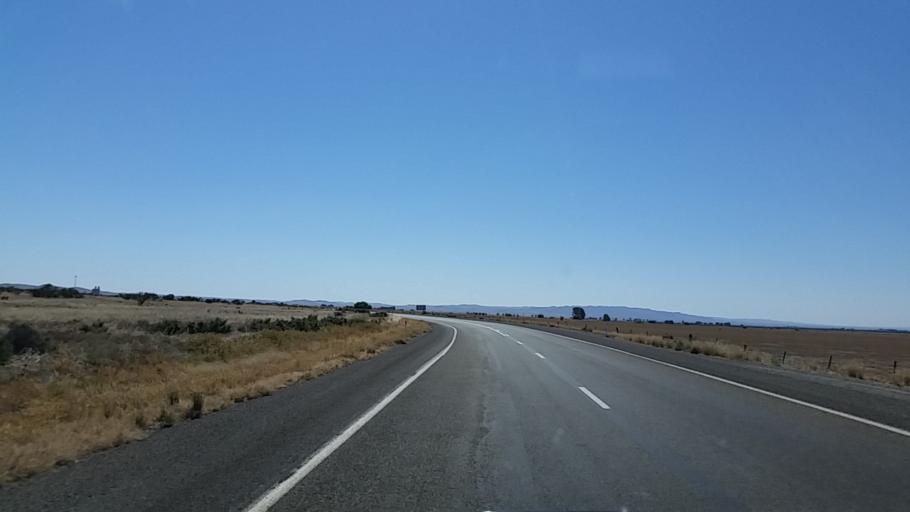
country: AU
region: South Australia
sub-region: Peterborough
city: Peterborough
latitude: -32.7473
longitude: 138.6365
